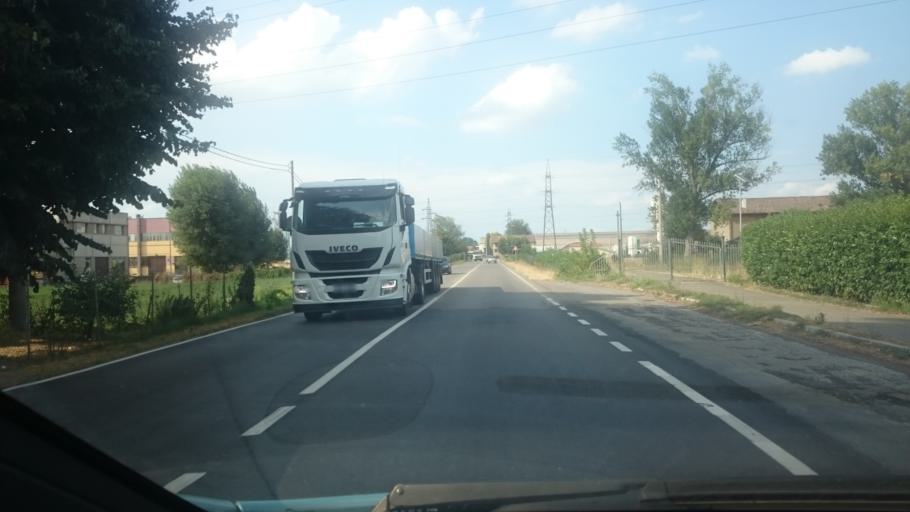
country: IT
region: Emilia-Romagna
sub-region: Provincia di Reggio Emilia
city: Salvaterra
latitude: 44.6229
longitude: 10.7773
